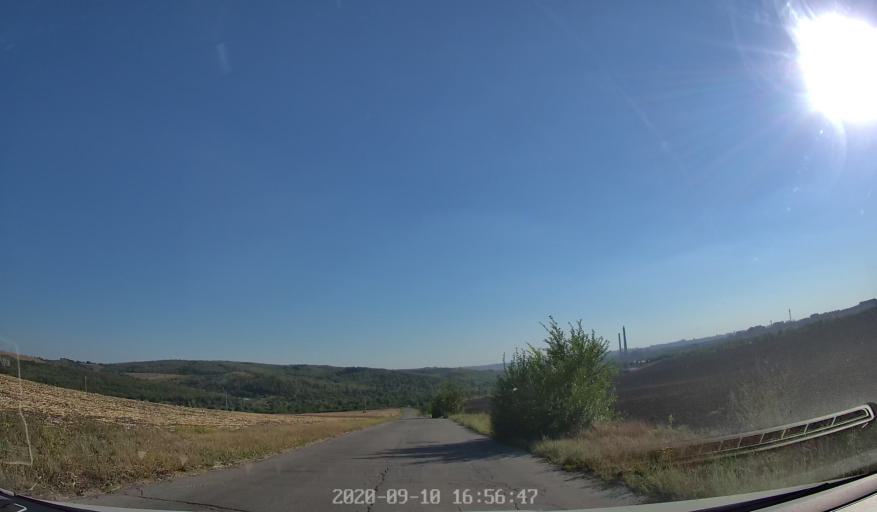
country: MD
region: Chisinau
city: Stauceni
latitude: 47.0541
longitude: 28.9167
